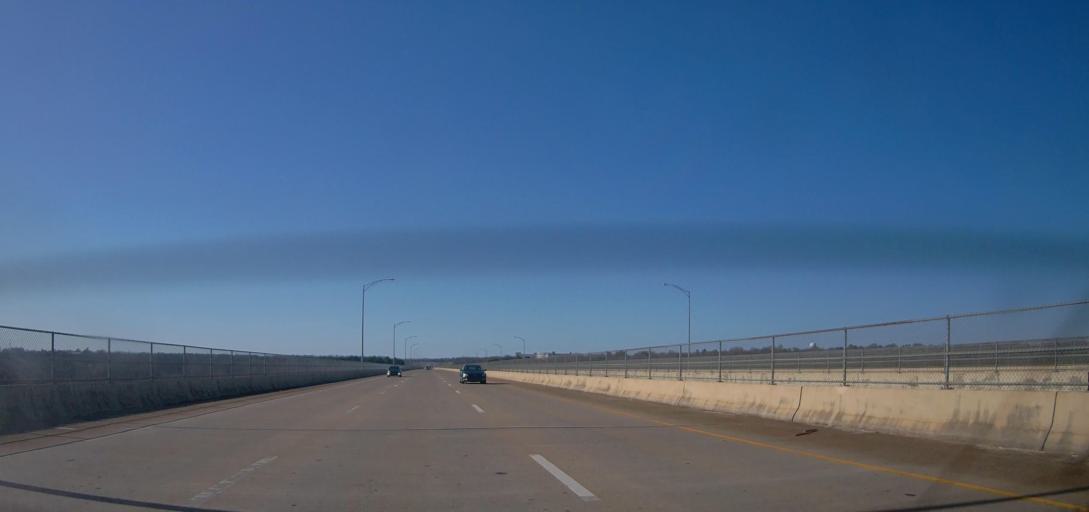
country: US
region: Alabama
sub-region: Lauderdale County
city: East Florence
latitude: 34.7920
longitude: -87.6430
